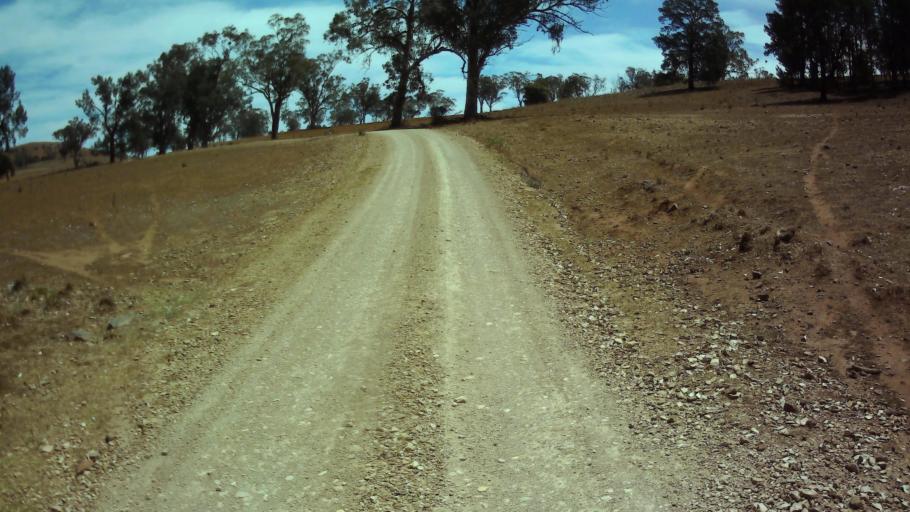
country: AU
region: New South Wales
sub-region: Weddin
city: Grenfell
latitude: -33.7445
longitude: 148.1728
